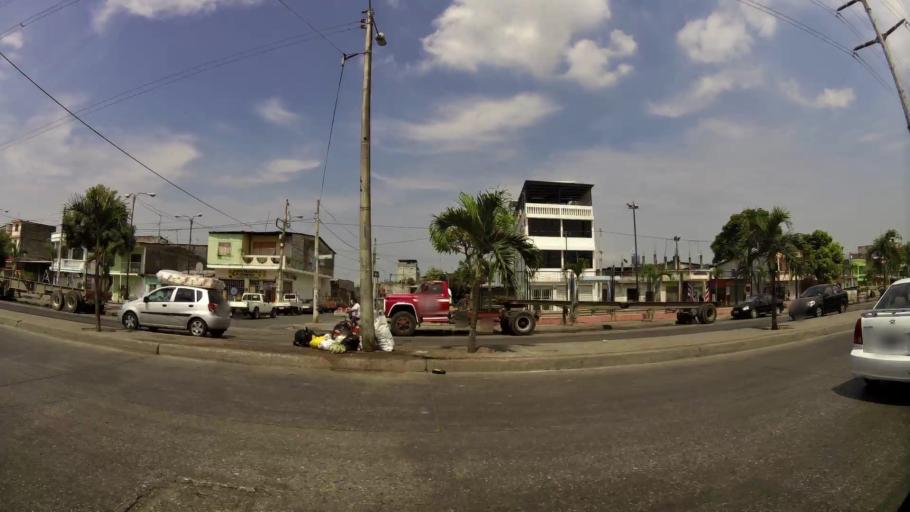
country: EC
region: Guayas
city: Guayaquil
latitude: -2.2604
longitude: -79.8810
